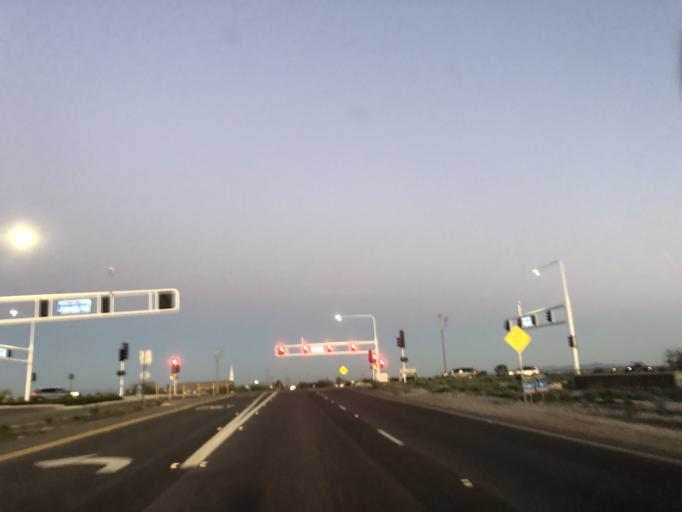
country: US
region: Arizona
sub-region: Maricopa County
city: Citrus Park
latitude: 33.4937
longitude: -112.4797
